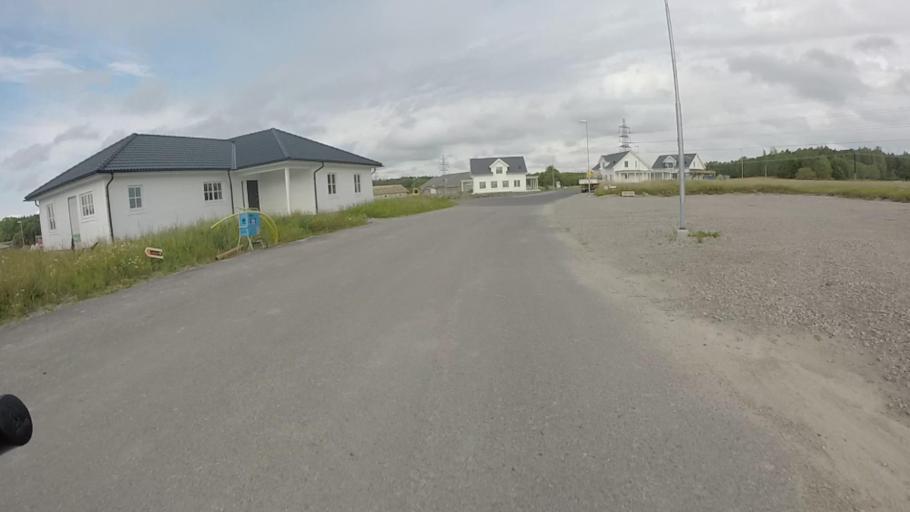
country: SE
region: Vaestra Goetaland
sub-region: Trollhattan
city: Trollhattan
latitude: 58.2777
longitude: 12.2530
